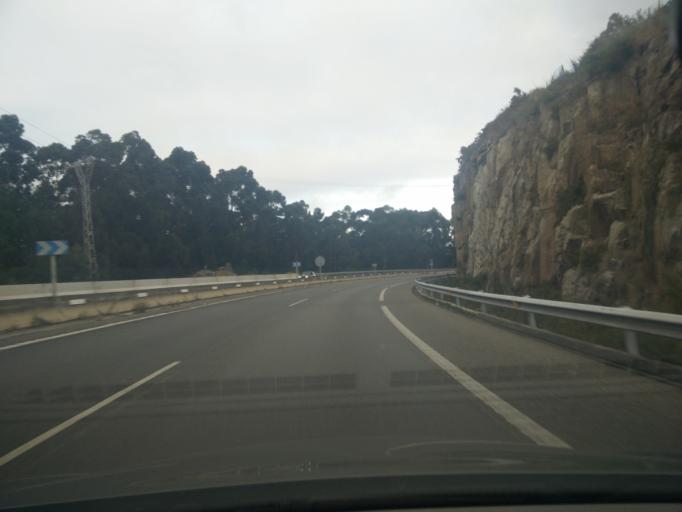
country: ES
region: Galicia
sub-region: Provincia da Coruna
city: Arteixo
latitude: 43.3380
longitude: -8.4548
